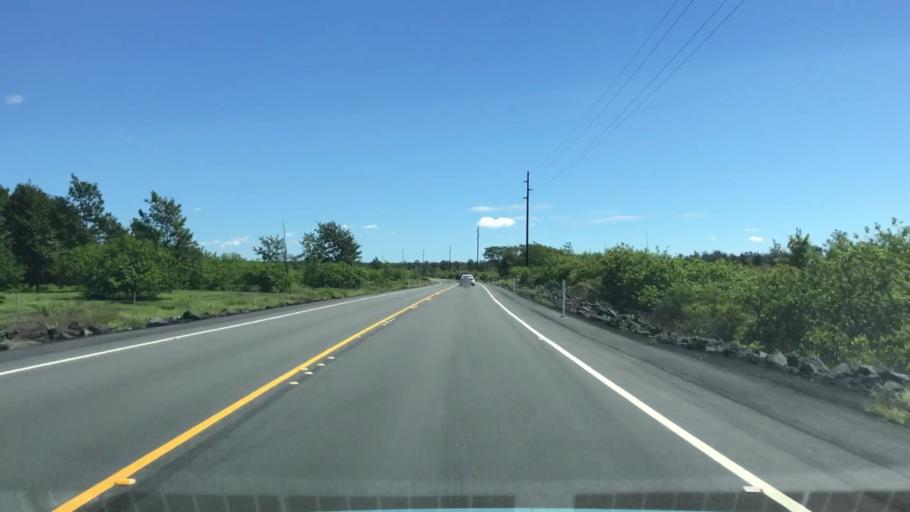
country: US
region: Hawaii
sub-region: Hawaii County
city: Pahala
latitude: 19.2752
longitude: -155.4315
